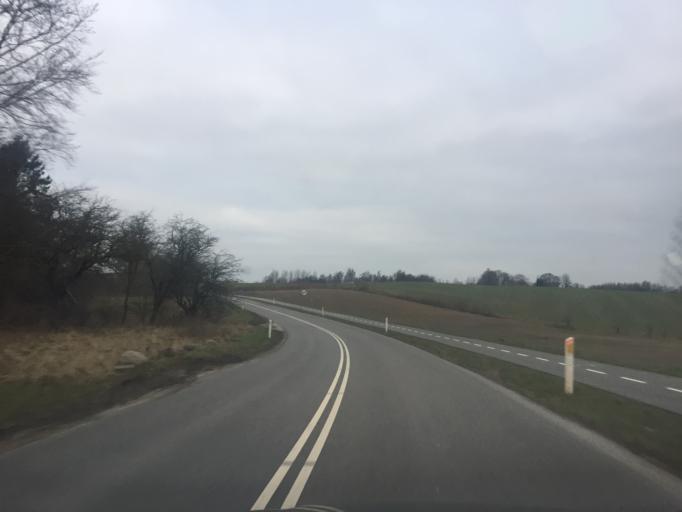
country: DK
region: Zealand
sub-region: Roskilde Kommune
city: Gundsomagle
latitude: 55.7523
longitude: 12.1371
